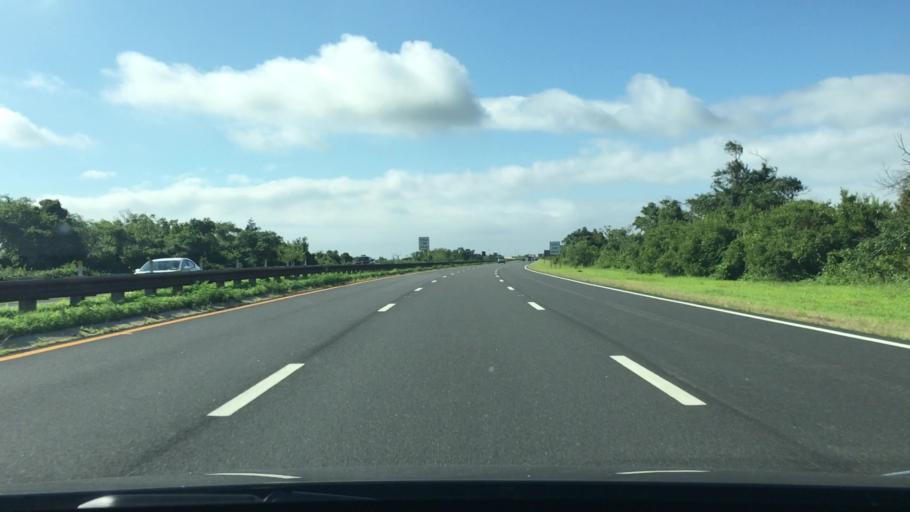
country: US
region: New York
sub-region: Nassau County
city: Seaford
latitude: 40.6329
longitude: -73.5035
